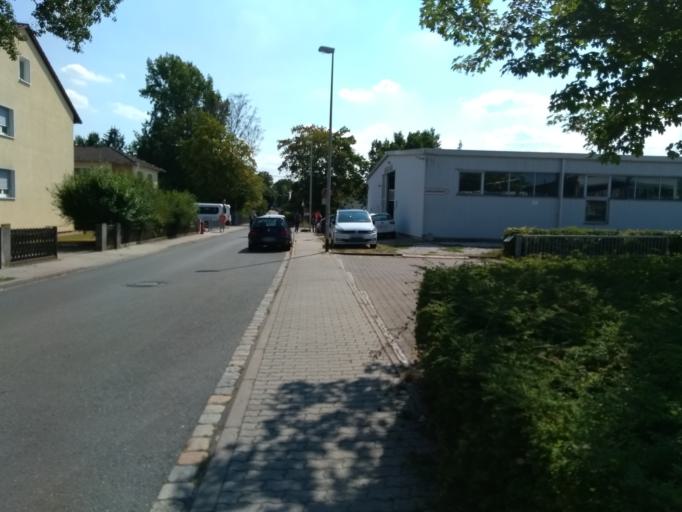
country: DE
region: Bavaria
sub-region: Regierungsbezirk Mittelfranken
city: Erlangen
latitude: 49.5715
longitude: 10.9986
